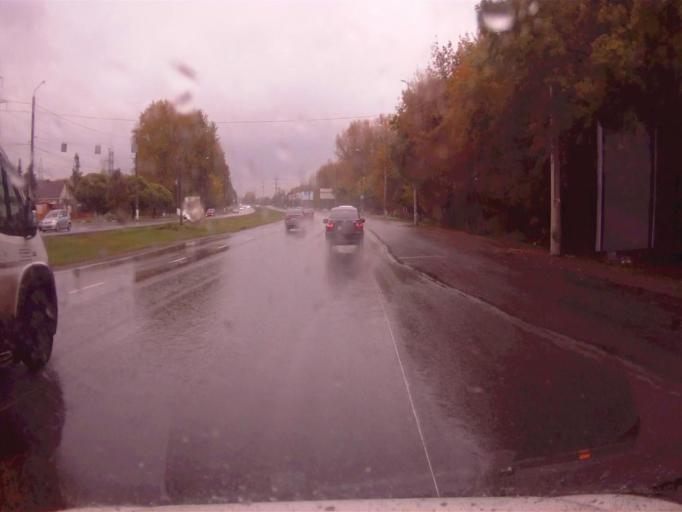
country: RU
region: Chelyabinsk
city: Dolgoderevenskoye
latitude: 55.2420
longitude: 61.3610
